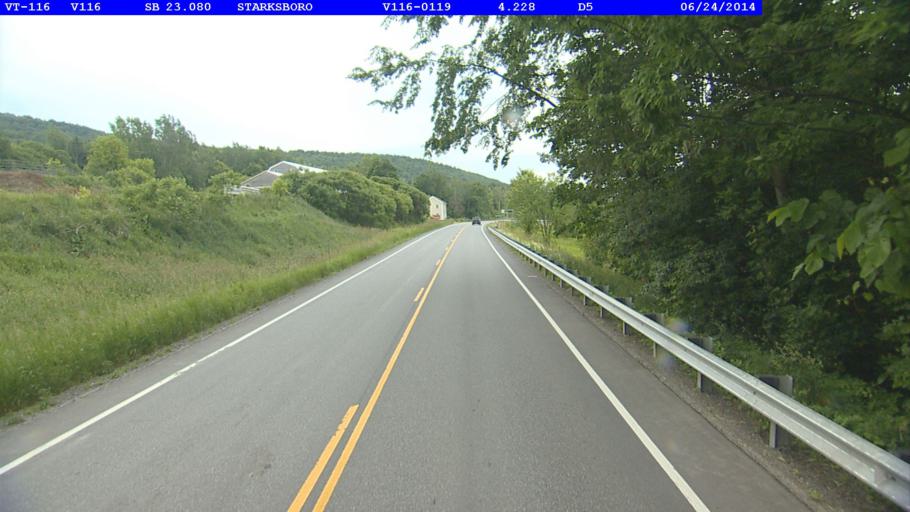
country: US
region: Vermont
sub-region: Chittenden County
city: Hinesburg
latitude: 44.2455
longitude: -73.0597
